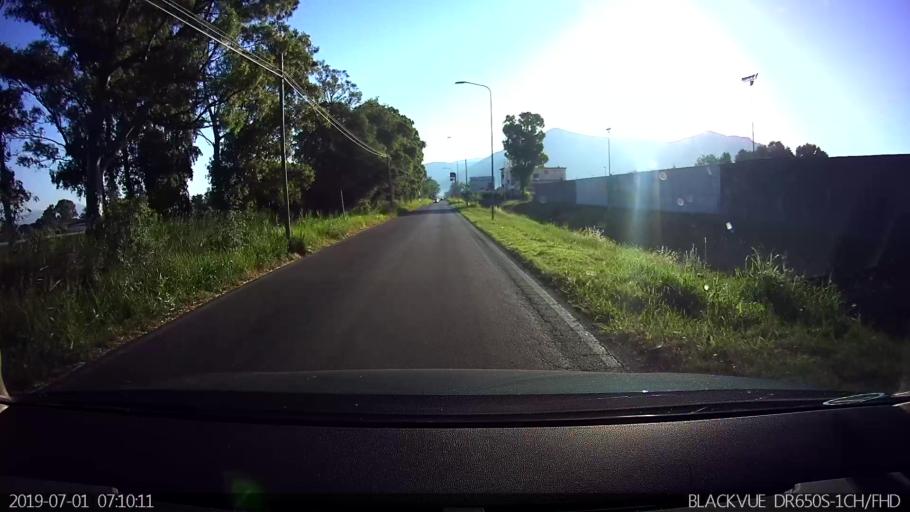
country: IT
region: Latium
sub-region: Provincia di Latina
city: Borgo Hermada
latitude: 41.3103
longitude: 13.1678
